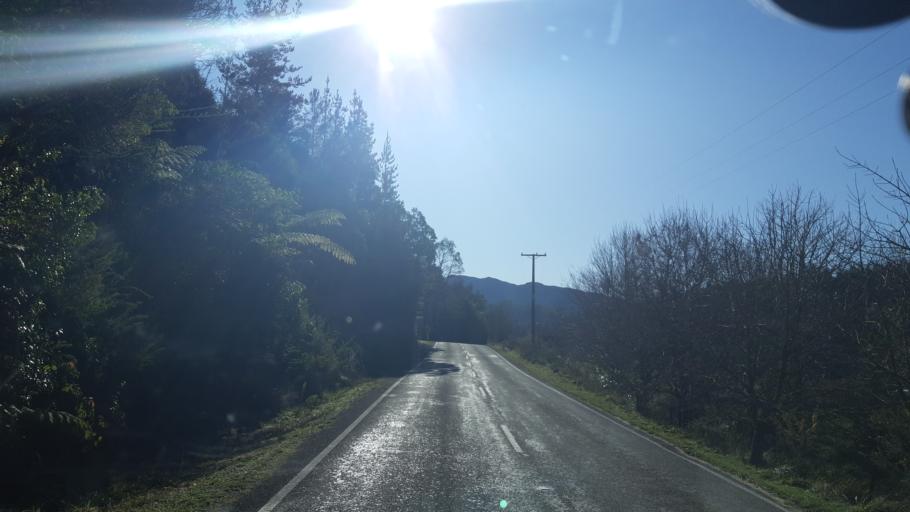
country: NZ
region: Tasman
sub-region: Tasman District
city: Motueka
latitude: -41.0245
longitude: 172.9797
